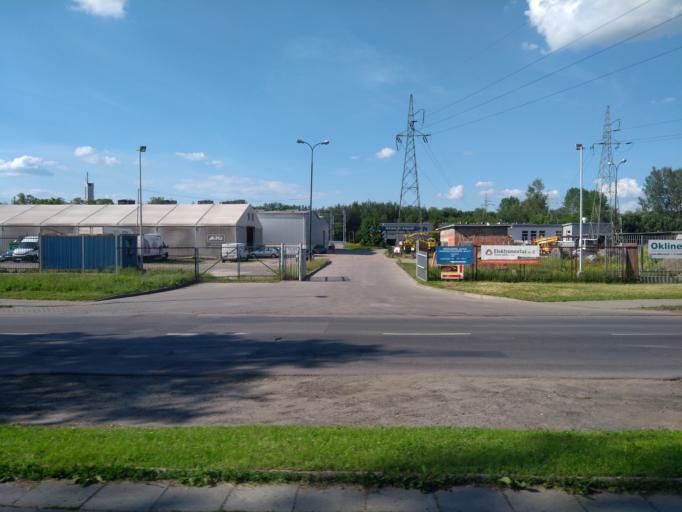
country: PL
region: Lesser Poland Voivodeship
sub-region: Powiat wielicki
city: Kokotow
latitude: 50.0879
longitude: 20.0603
